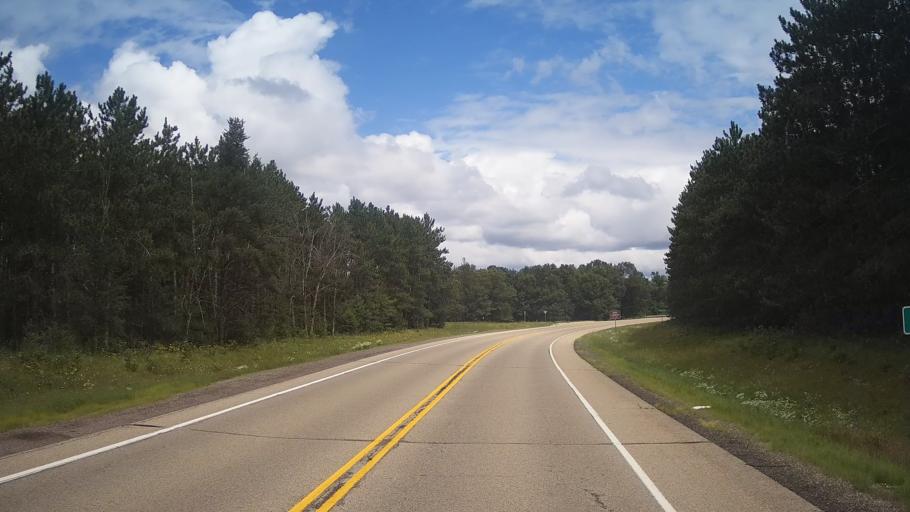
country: US
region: Wisconsin
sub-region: Juneau County
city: New Lisbon
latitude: 44.0452
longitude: -90.0249
